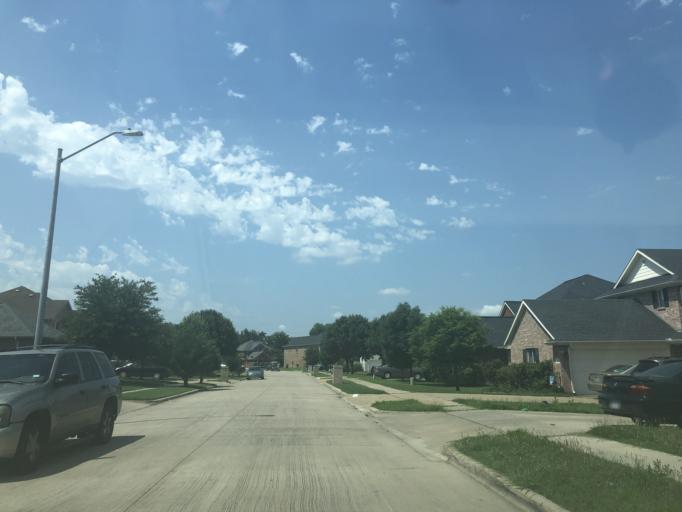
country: US
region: Texas
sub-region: Dallas County
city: Grand Prairie
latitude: 32.7264
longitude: -97.0014
